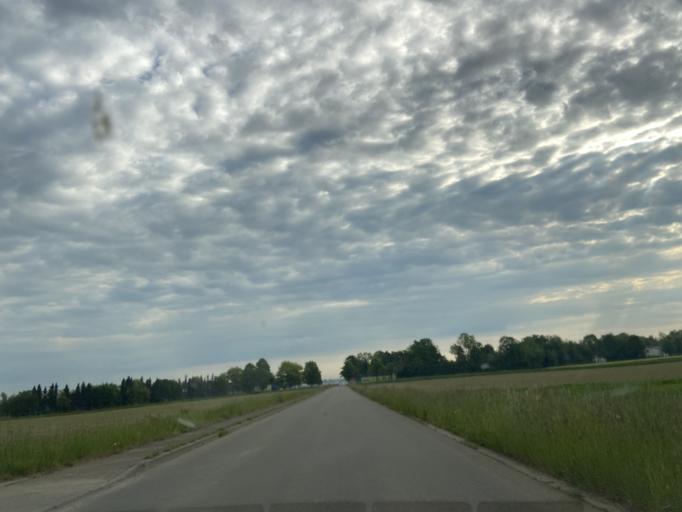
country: DE
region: Baden-Wuerttemberg
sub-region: Tuebingen Region
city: Hohentengen
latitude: 48.0435
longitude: 9.3644
